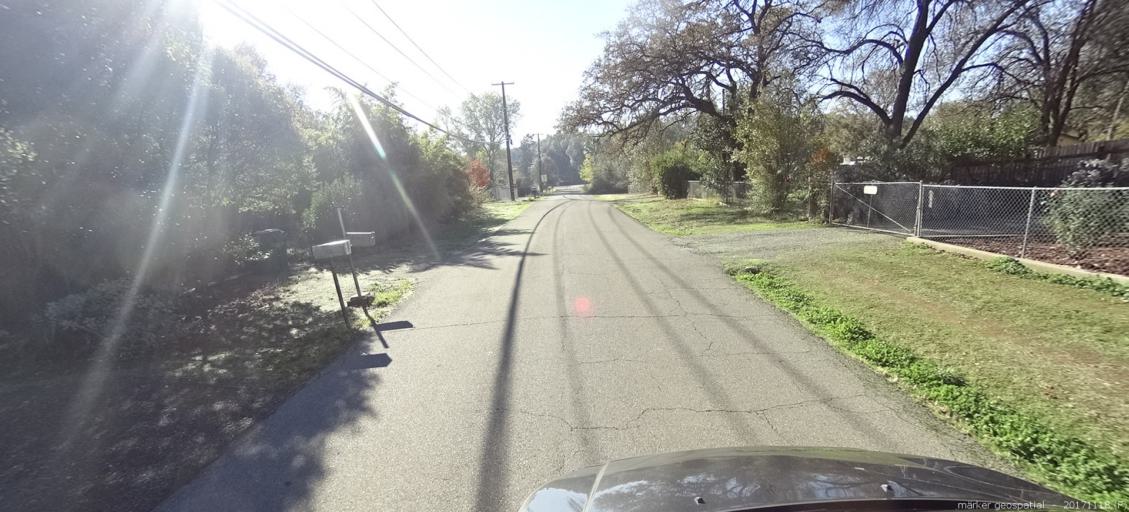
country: US
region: California
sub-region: Shasta County
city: Cottonwood
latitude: 40.3871
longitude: -122.3146
